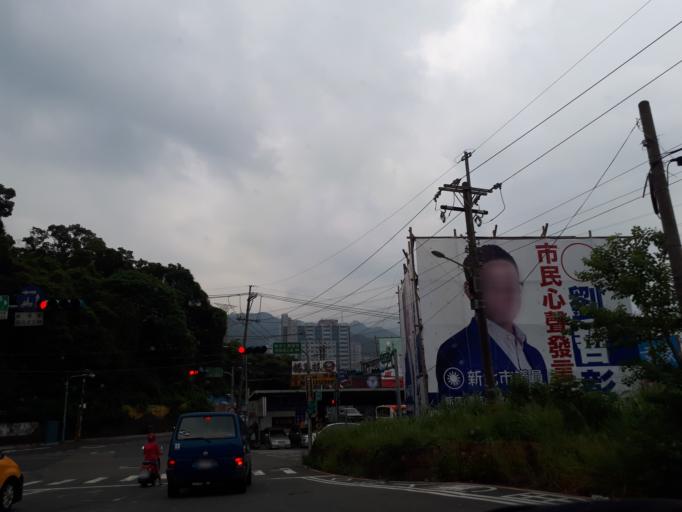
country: TW
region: Taipei
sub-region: Taipei
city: Banqiao
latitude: 24.9583
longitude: 121.5047
